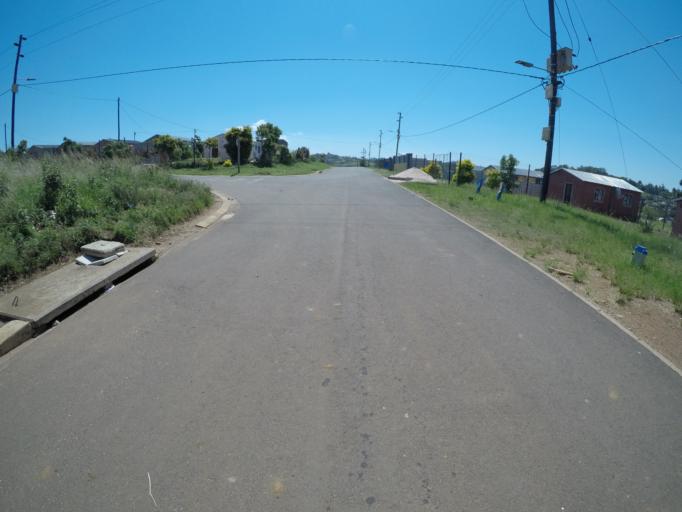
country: ZA
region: KwaZulu-Natal
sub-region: uThungulu District Municipality
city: Empangeni
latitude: -28.7655
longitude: 31.8818
